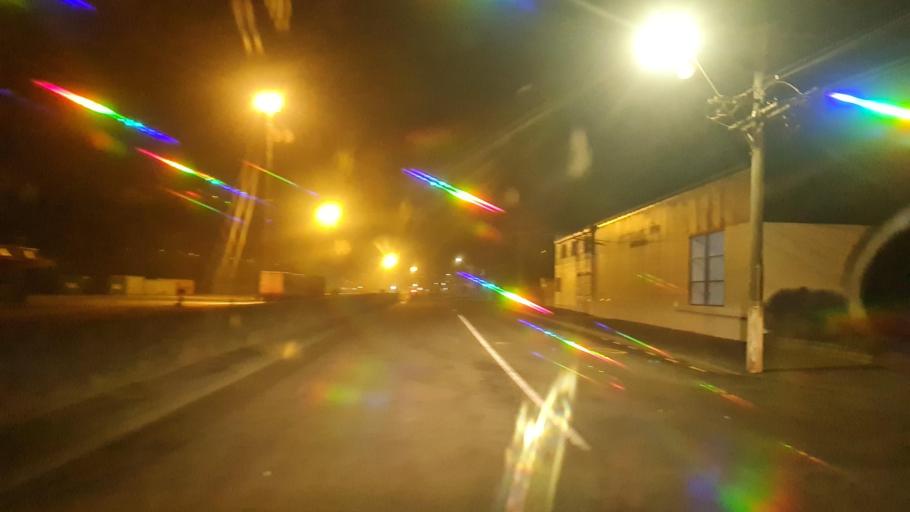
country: NZ
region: Otago
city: Oamaru
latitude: -45.0909
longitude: 170.9790
